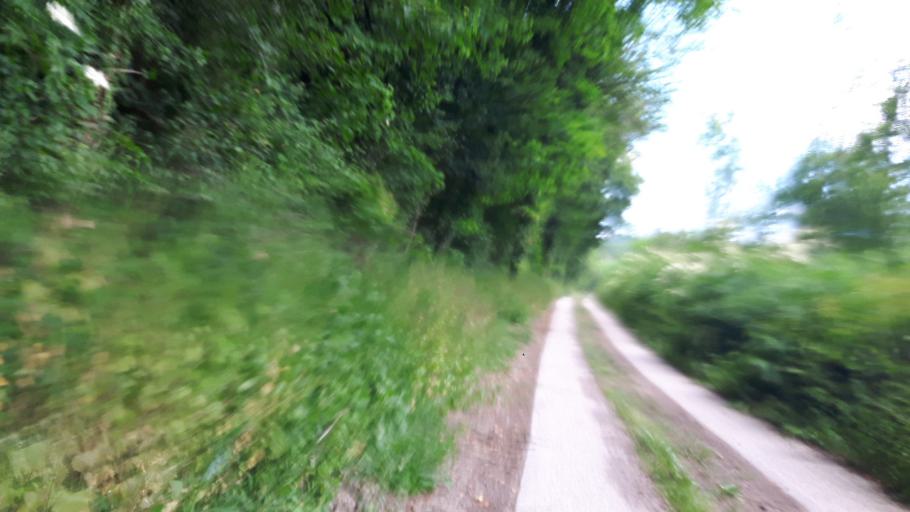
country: DE
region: Baden-Wuerttemberg
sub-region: Regierungsbezirk Stuttgart
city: Jagsthausen
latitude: 49.2821
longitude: 9.4556
